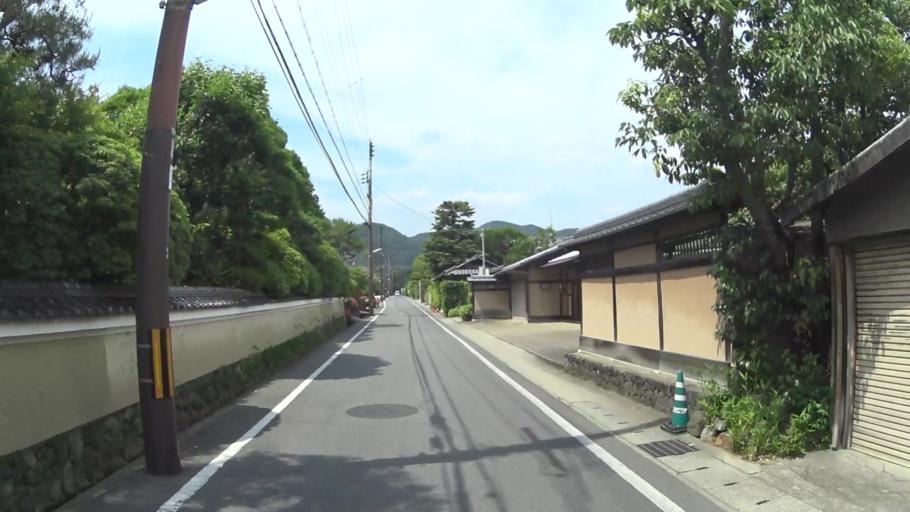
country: JP
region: Kyoto
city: Muko
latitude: 35.0245
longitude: 135.6789
